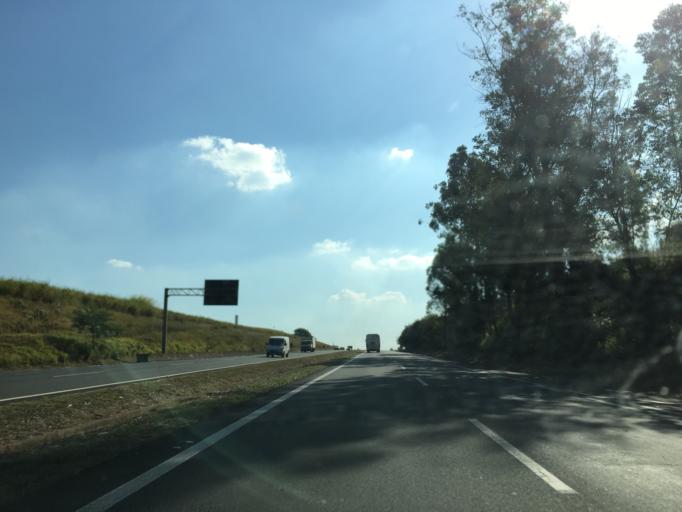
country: BR
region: Sao Paulo
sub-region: Santa Barbara D'Oeste
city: Santa Barbara d'Oeste
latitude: -22.7639
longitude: -47.4508
